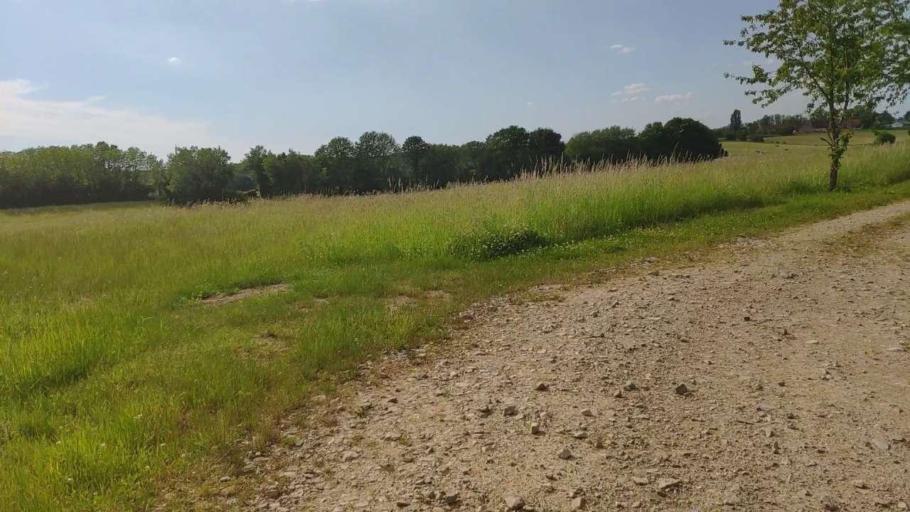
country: FR
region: Bourgogne
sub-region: Departement de Saone-et-Loire
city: Saint-Germain-du-Bois
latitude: 46.8074
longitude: 5.3388
